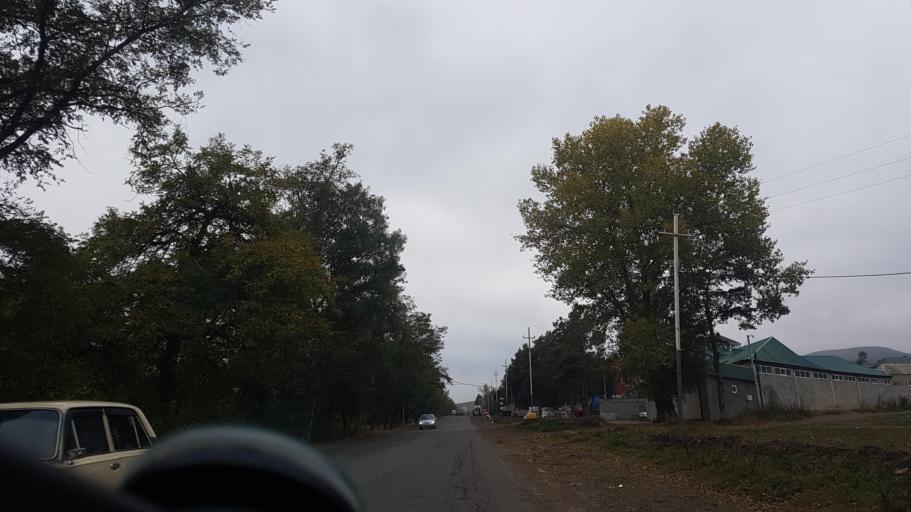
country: AZ
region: Gadabay Rayon
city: Ariqdam
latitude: 40.6435
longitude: 45.8128
